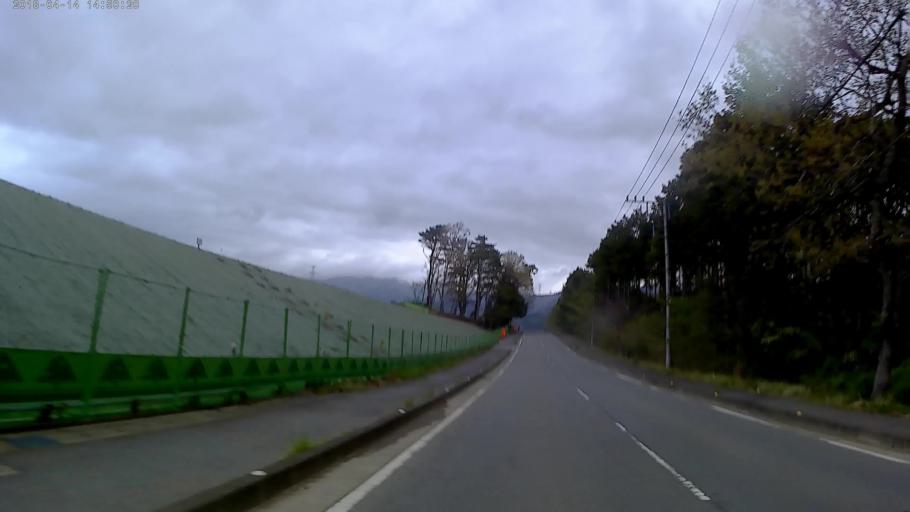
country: JP
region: Shizuoka
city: Gotemba
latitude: 35.3649
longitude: 138.9670
